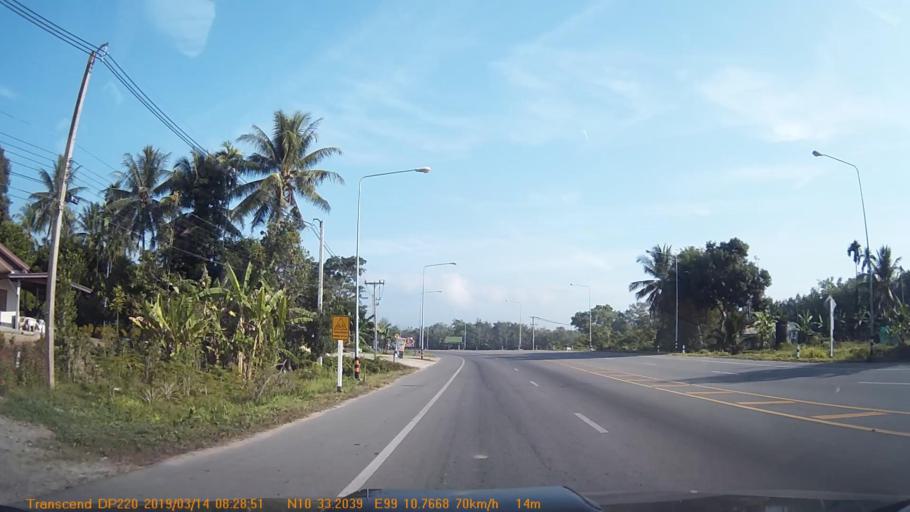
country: TH
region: Chumphon
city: Chumphon
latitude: 10.5536
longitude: 99.1794
